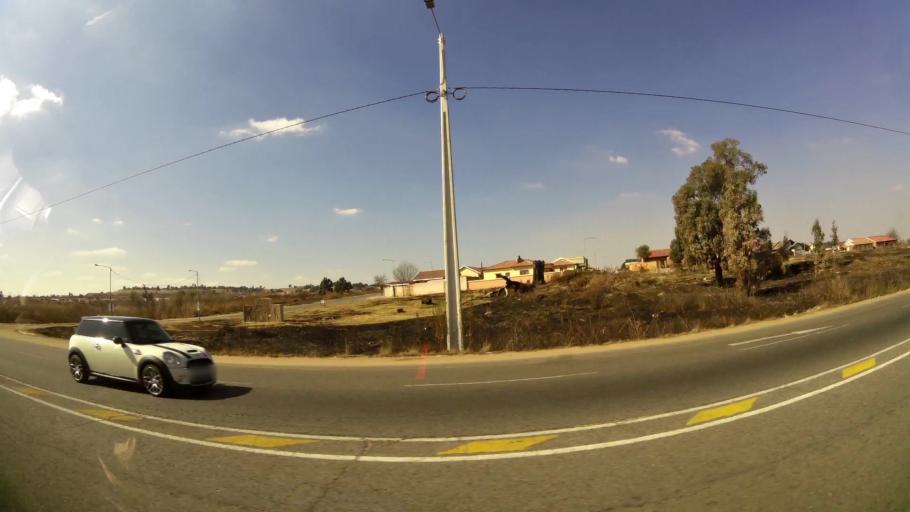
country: ZA
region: Gauteng
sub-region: West Rand District Municipality
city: Krugersdorp
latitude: -26.1503
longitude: 27.7631
